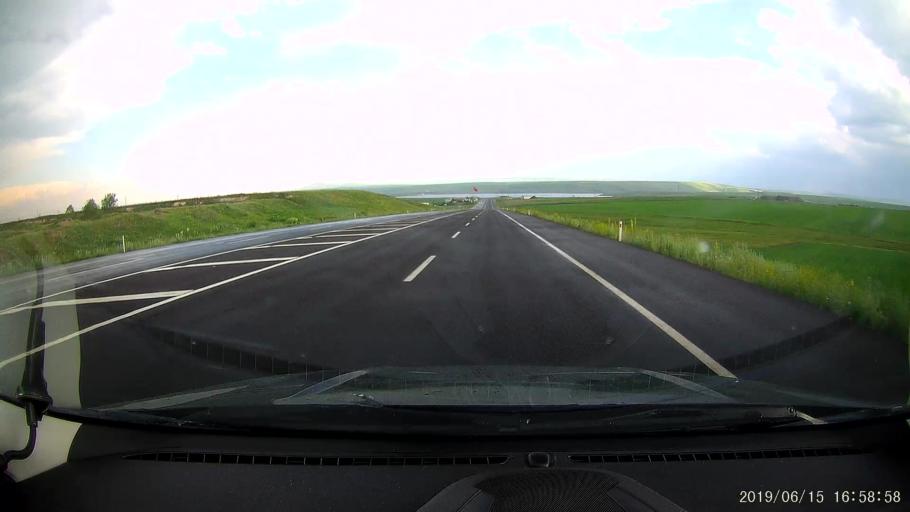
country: TR
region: Kars
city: Susuz
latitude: 40.7580
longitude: 43.1471
